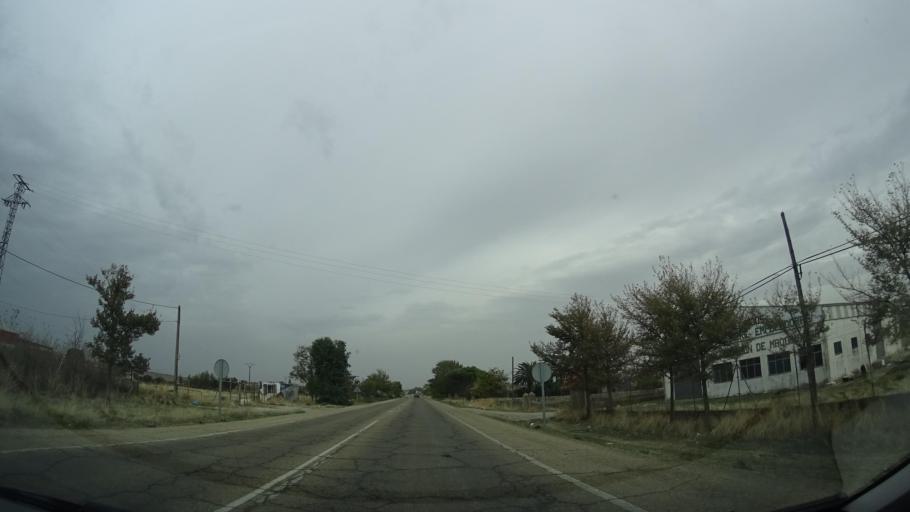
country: ES
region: Extremadura
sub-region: Provincia de Caceres
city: Trujillo
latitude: 39.4649
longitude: -5.8654
